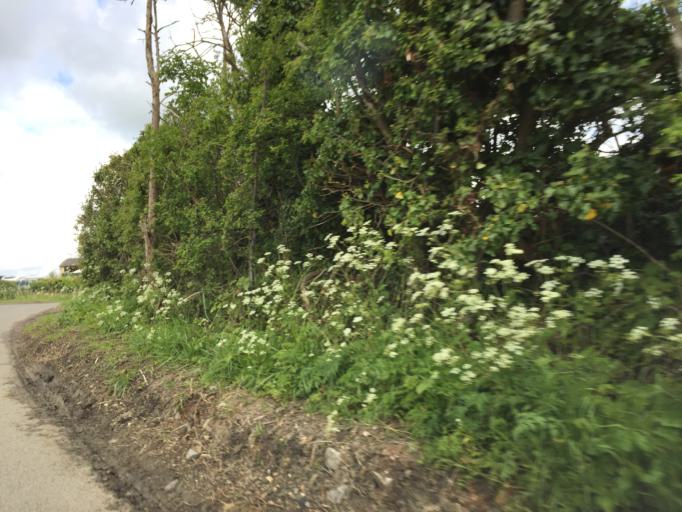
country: GB
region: England
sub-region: Gloucestershire
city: Stonehouse
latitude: 51.7747
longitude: -2.2988
